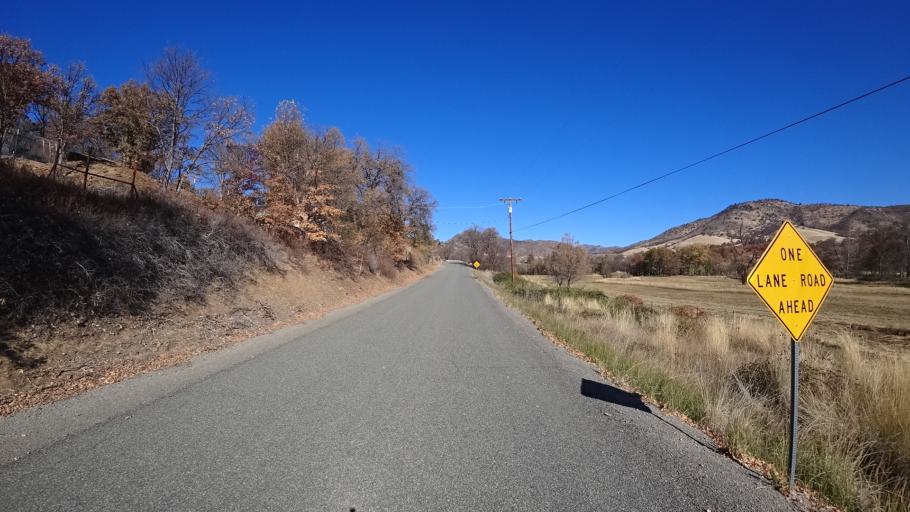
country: US
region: California
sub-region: Siskiyou County
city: Yreka
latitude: 41.9393
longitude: -122.5915
